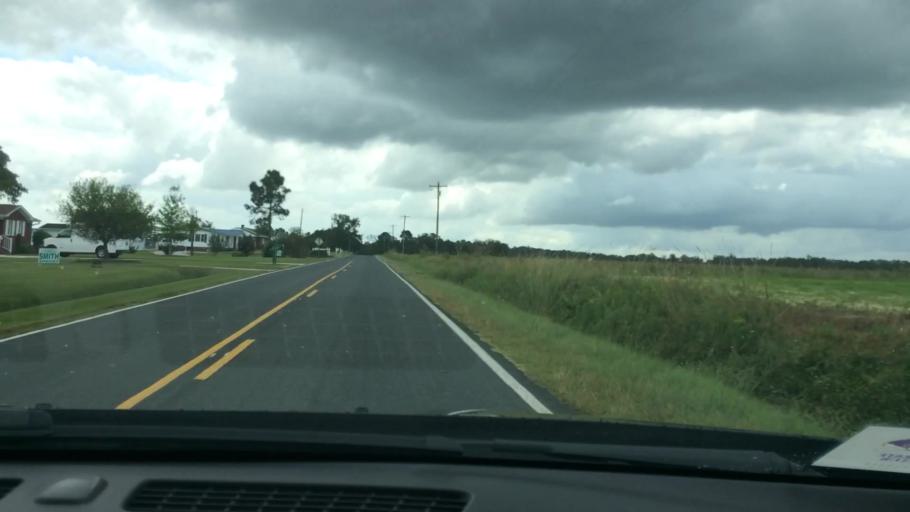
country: US
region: North Carolina
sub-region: Greene County
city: Maury
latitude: 35.5140
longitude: -77.5255
